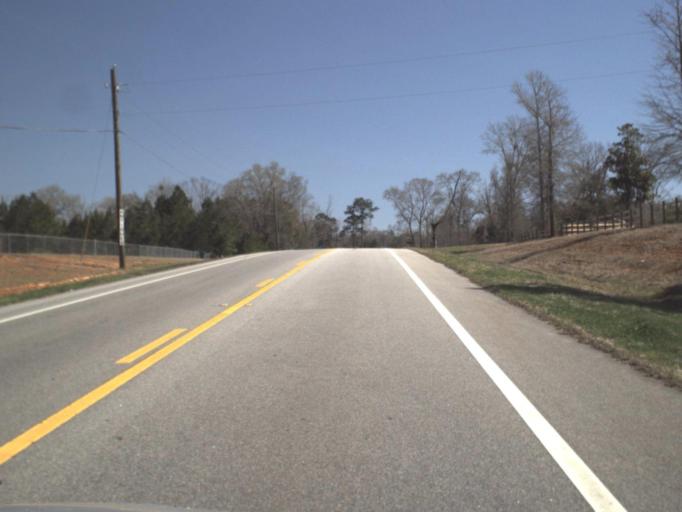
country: US
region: Florida
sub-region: Jackson County
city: Marianna
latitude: 30.8048
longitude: -85.2834
